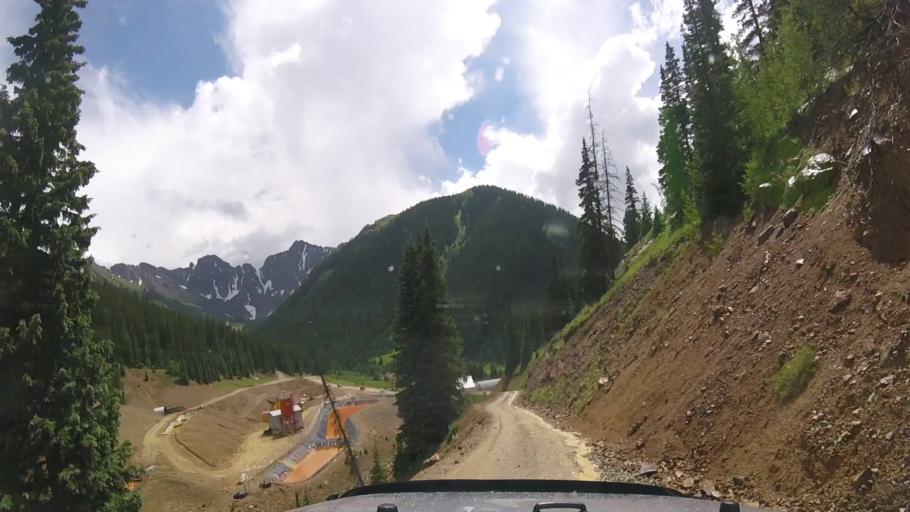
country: US
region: Colorado
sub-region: San Juan County
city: Silverton
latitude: 37.8923
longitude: -107.6491
